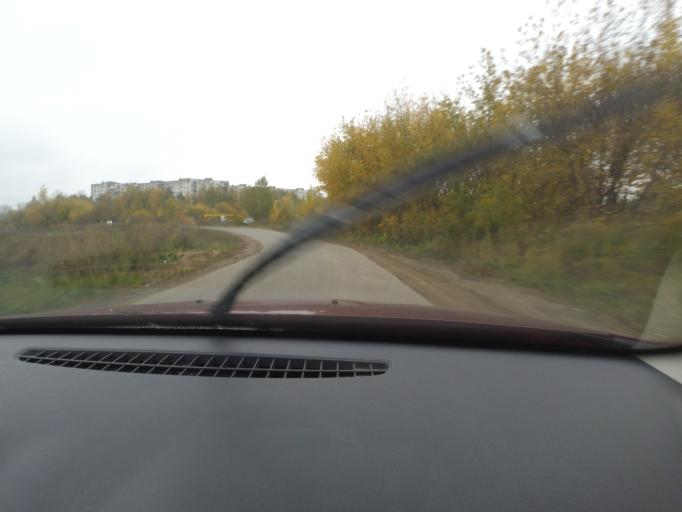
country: RU
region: Nizjnij Novgorod
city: Afonino
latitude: 56.2775
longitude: 44.0525
